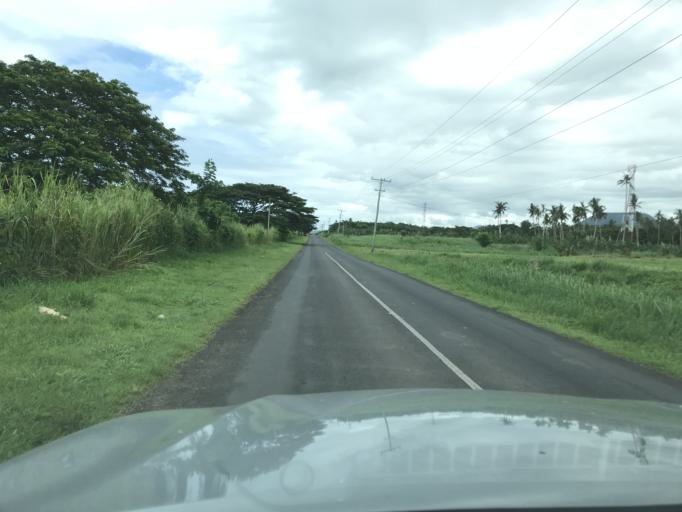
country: WS
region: Aiga-i-le-Tai
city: Mulifanua
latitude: -13.8329
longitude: -172.0248
